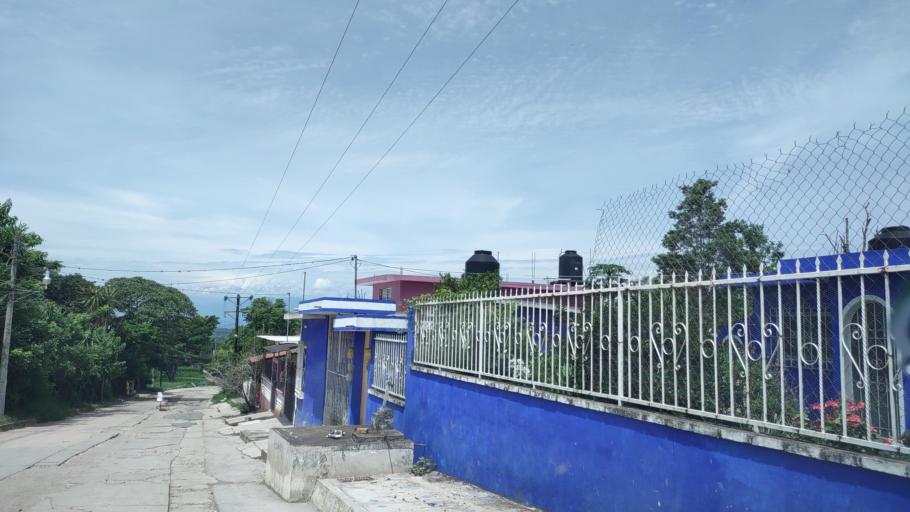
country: MX
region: Veracruz
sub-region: Emiliano Zapata
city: Jacarandas
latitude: 19.4679
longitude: -96.8318
